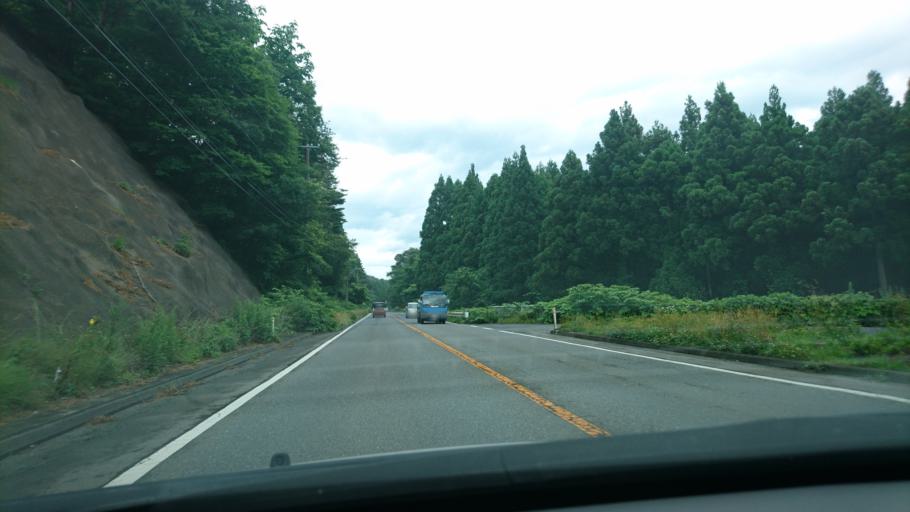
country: JP
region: Iwate
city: Yamada
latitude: 39.4095
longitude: 141.9607
